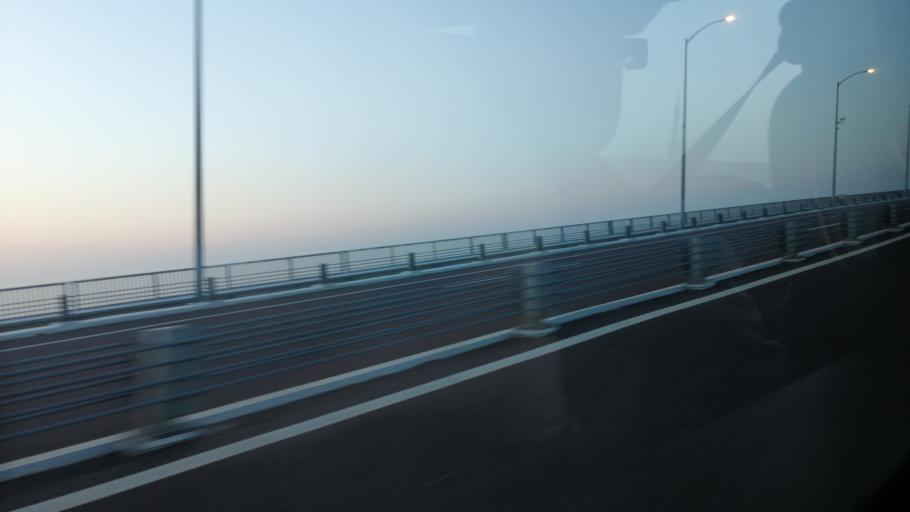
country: TR
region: Yalova
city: Altinova
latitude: 40.7400
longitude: 29.5135
